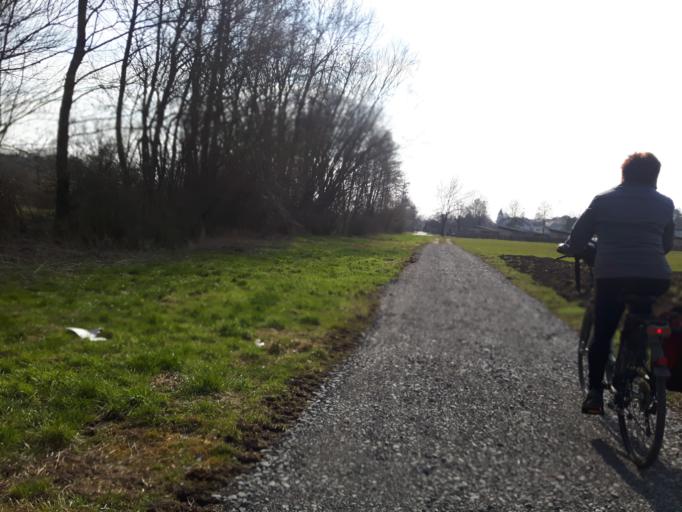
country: DE
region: Baden-Wuerttemberg
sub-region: Regierungsbezirk Stuttgart
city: Schwaigern
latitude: 49.1340
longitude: 9.0176
